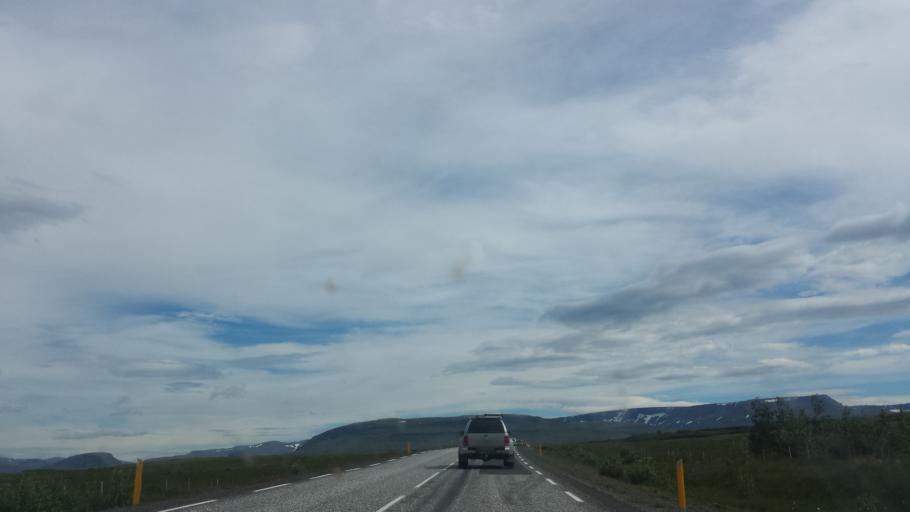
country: IS
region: West
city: Borgarnes
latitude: 64.3713
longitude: -21.8358
